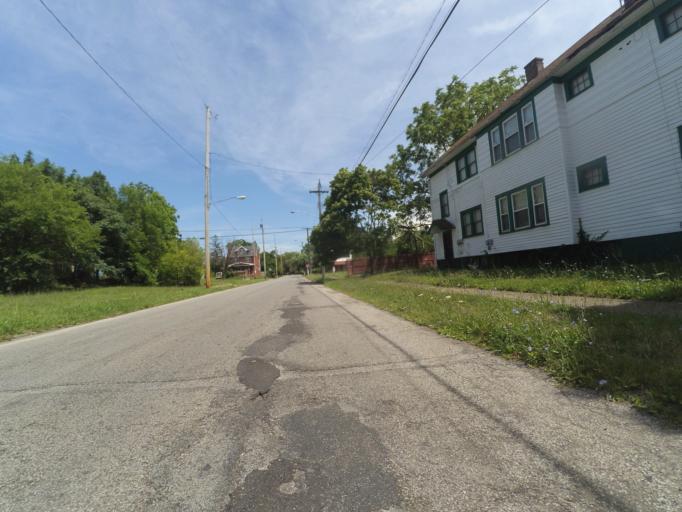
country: US
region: Ohio
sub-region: Cuyahoga County
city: Garfield Heights
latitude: 41.4592
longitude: -81.6105
